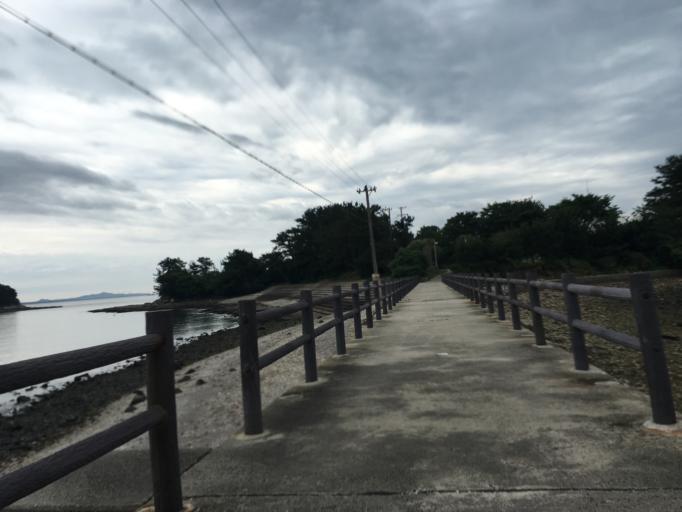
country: JP
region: Aichi
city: Ishiki
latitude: 34.7185
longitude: 137.0456
